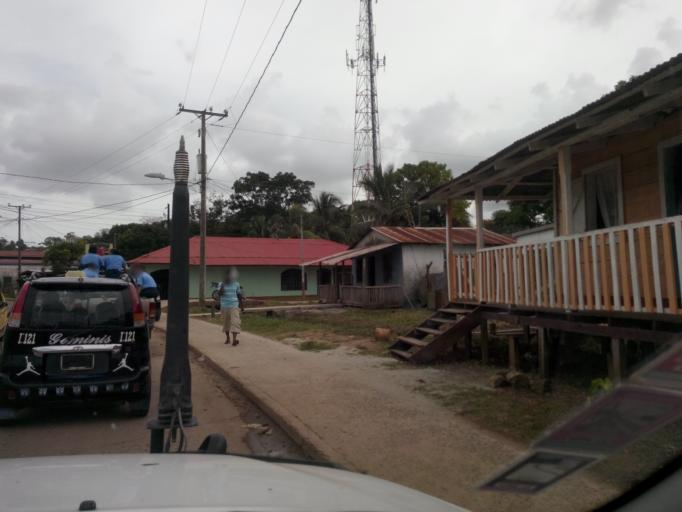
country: NI
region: Atlantico Sur
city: Bluefields
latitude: 12.0266
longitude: -83.7677
